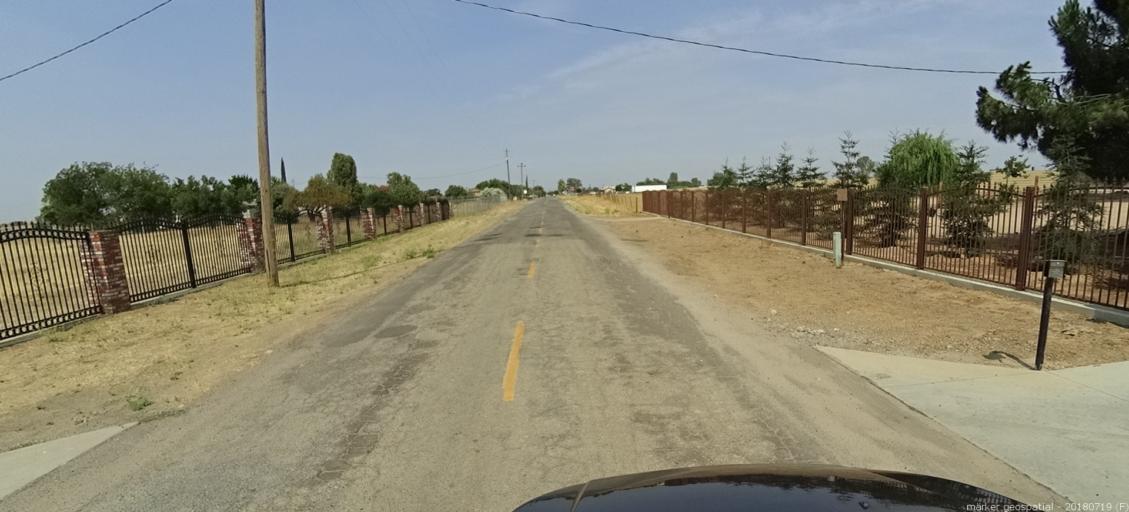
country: US
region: California
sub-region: Madera County
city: Fairmead
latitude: 37.0764
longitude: -120.1824
